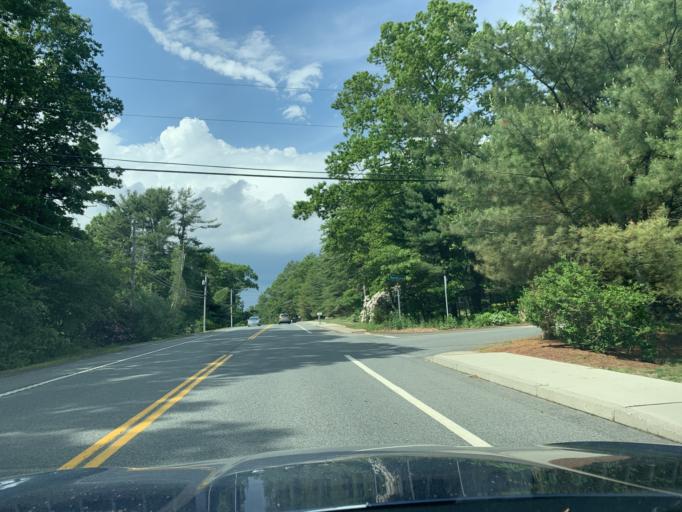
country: US
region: Rhode Island
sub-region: Kent County
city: Coventry
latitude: 41.6863
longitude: -71.6934
